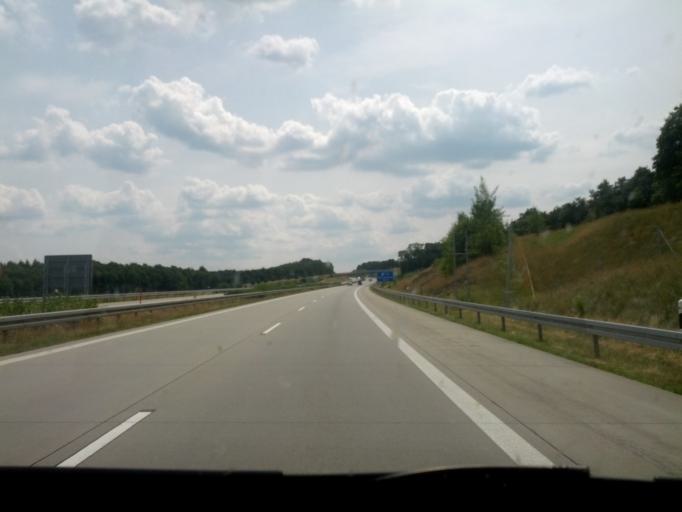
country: DE
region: Saxony
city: Liebstadt
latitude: 50.8465
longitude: 13.8812
